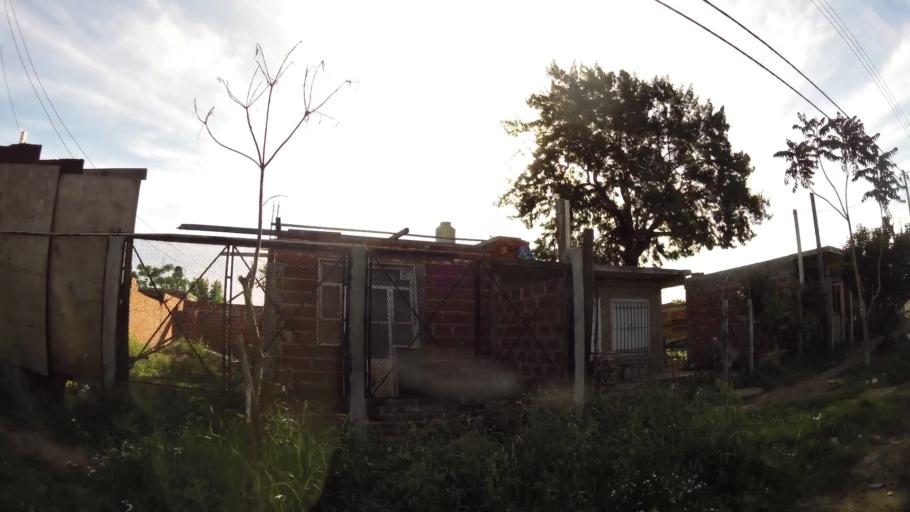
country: AR
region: Buenos Aires
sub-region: Partido de Almirante Brown
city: Adrogue
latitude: -34.8157
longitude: -58.3253
